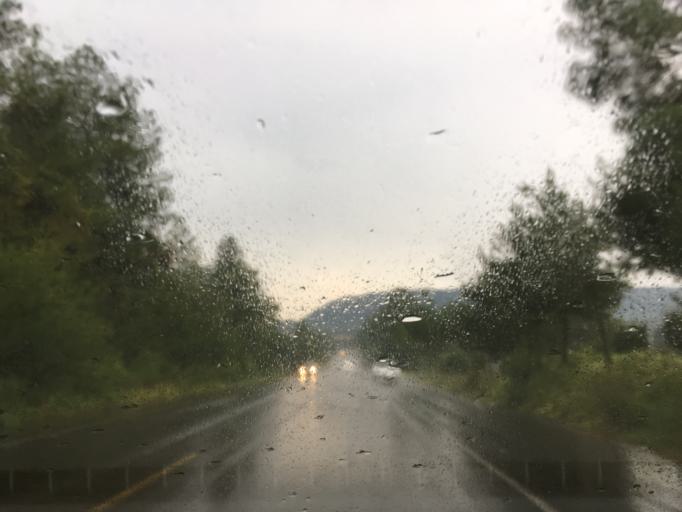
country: MX
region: Michoacan
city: Angahuan
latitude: 19.5444
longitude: -102.2076
